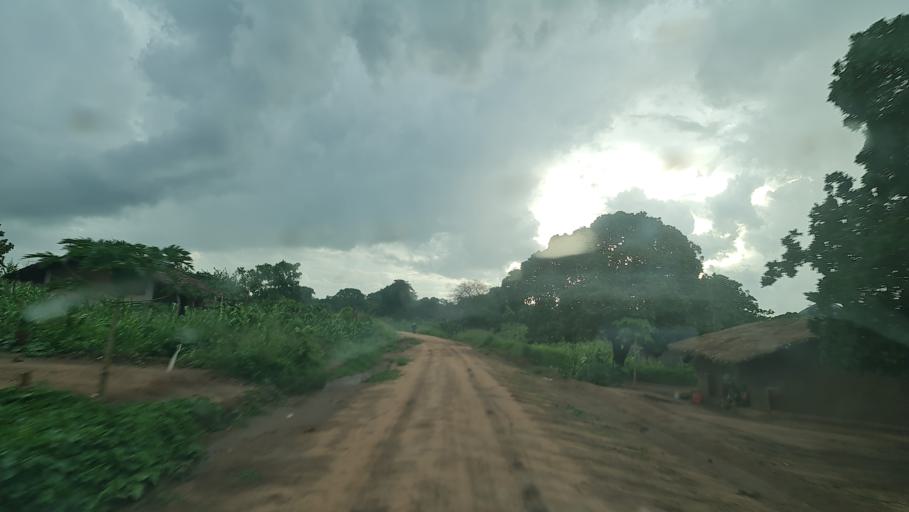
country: MZ
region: Nampula
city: Nacala
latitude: -13.9915
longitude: 40.3697
